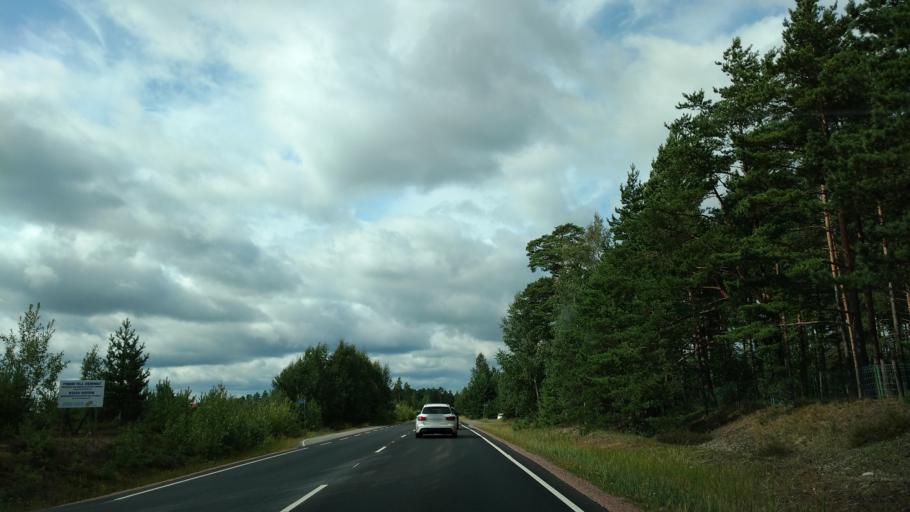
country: FI
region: Varsinais-Suomi
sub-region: Salo
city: Saerkisalo
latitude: 60.1847
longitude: 22.8573
